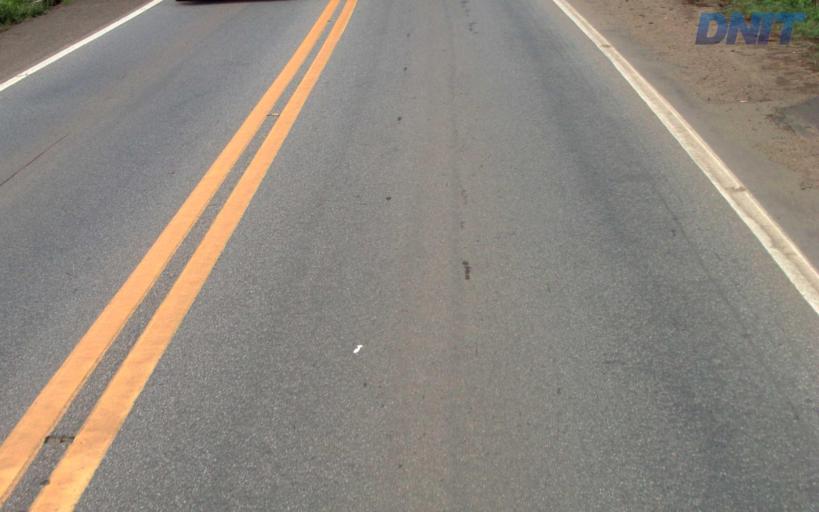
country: BR
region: Minas Gerais
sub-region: Ipaba
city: Ipaba
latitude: -19.3670
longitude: -42.4503
